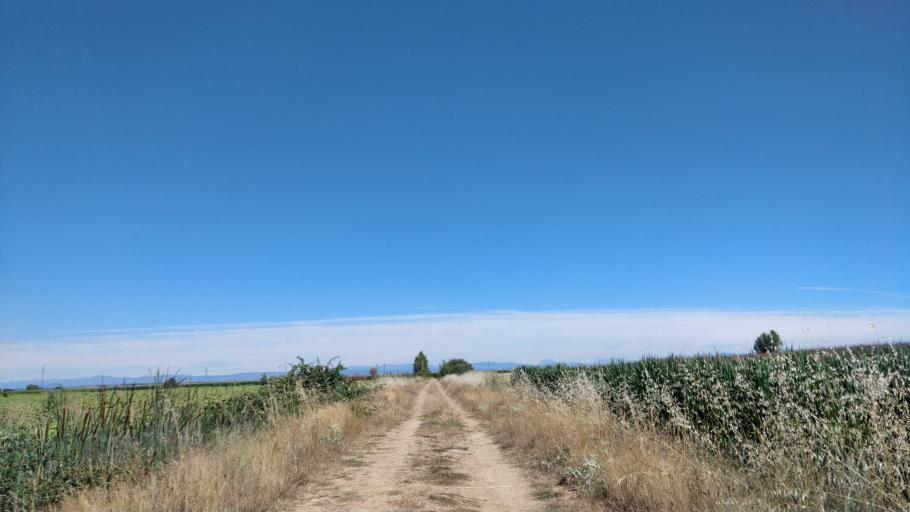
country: ES
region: Castille and Leon
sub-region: Provincia de Leon
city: Bustillo del Paramo
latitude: 42.4494
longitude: -5.8164
